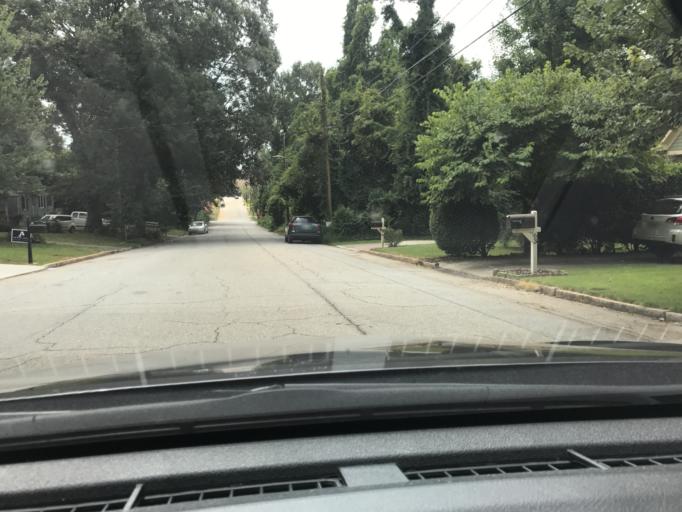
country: US
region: Georgia
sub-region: DeKalb County
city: Decatur
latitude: 33.7502
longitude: -84.3112
